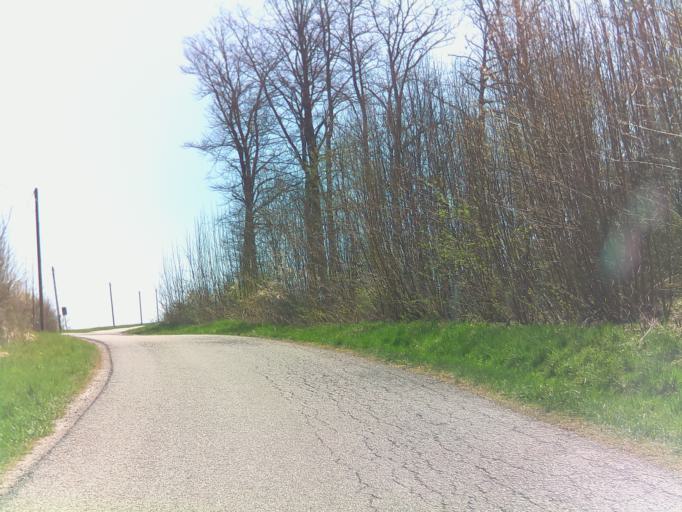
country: DE
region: Bavaria
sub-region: Upper Palatinate
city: Kastl
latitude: 49.3829
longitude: 11.6933
